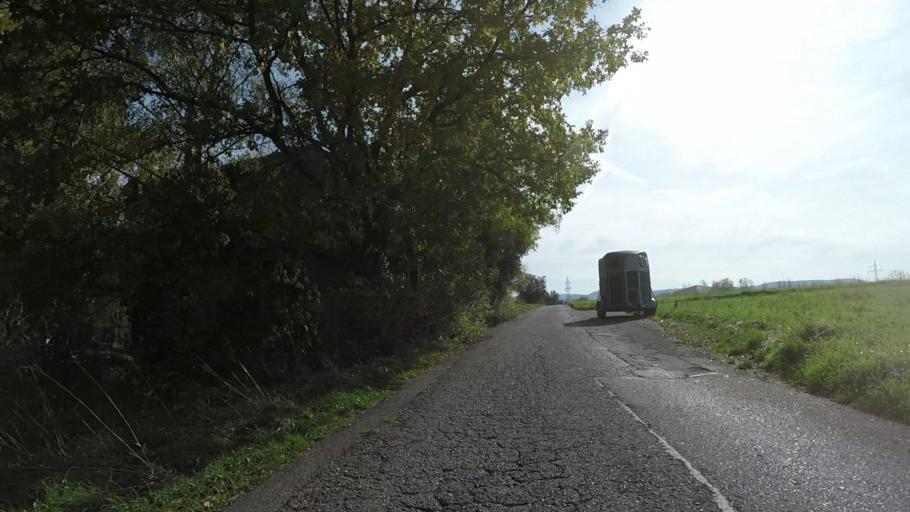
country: DE
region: Baden-Wuerttemberg
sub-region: Tuebingen Region
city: Wannweil
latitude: 48.5020
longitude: 9.1540
